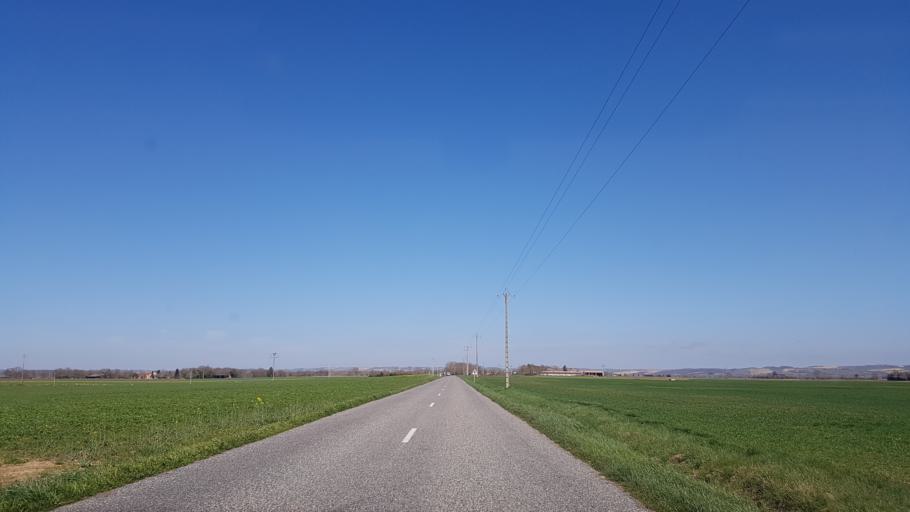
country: FR
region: Languedoc-Roussillon
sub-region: Departement de l'Aude
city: Belpech
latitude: 43.1699
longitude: 1.7099
